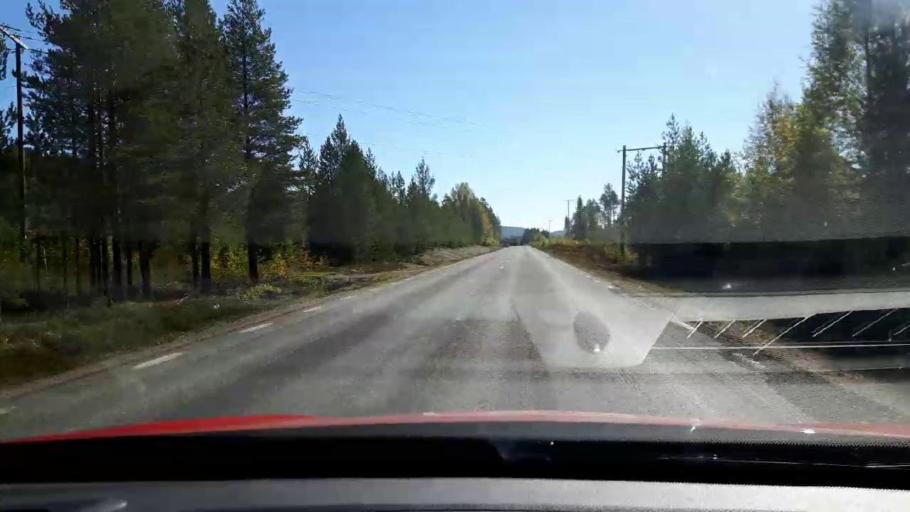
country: SE
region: Jaemtland
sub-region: Harjedalens Kommun
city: Sveg
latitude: 62.3058
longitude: 14.0508
